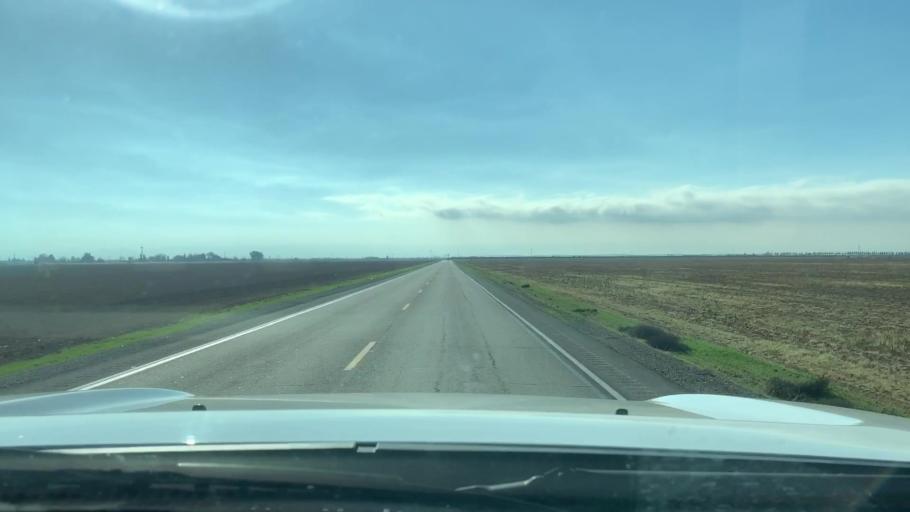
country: US
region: California
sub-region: Kern County
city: Rosedale
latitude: 35.4556
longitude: -119.1540
